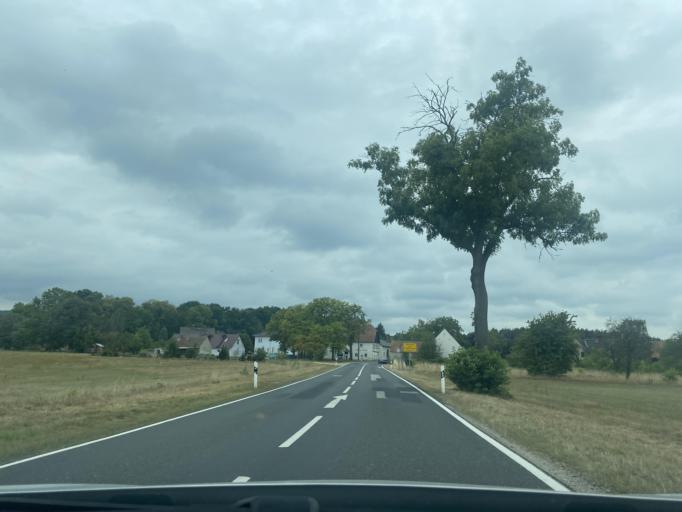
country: DE
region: Saxony
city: Mucka
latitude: 51.2820
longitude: 14.6983
